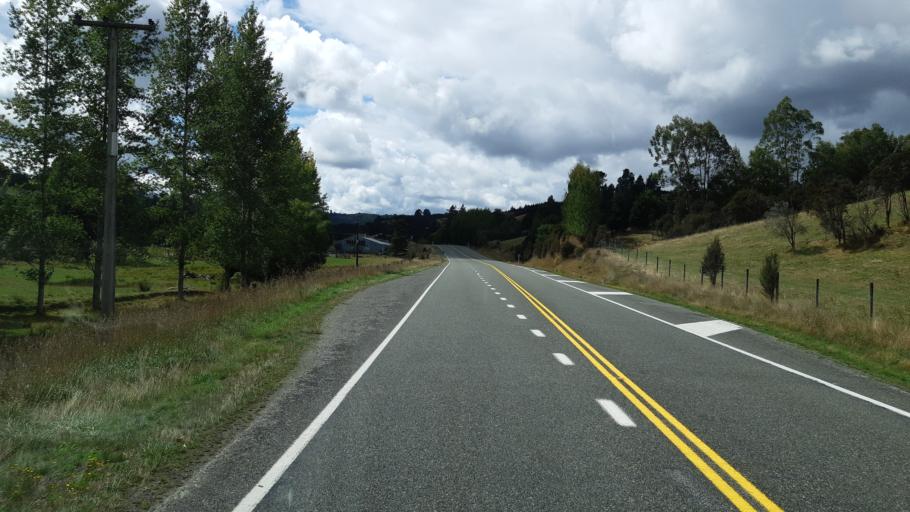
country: NZ
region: Tasman
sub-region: Tasman District
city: Wakefield
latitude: -41.6415
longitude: 172.6759
